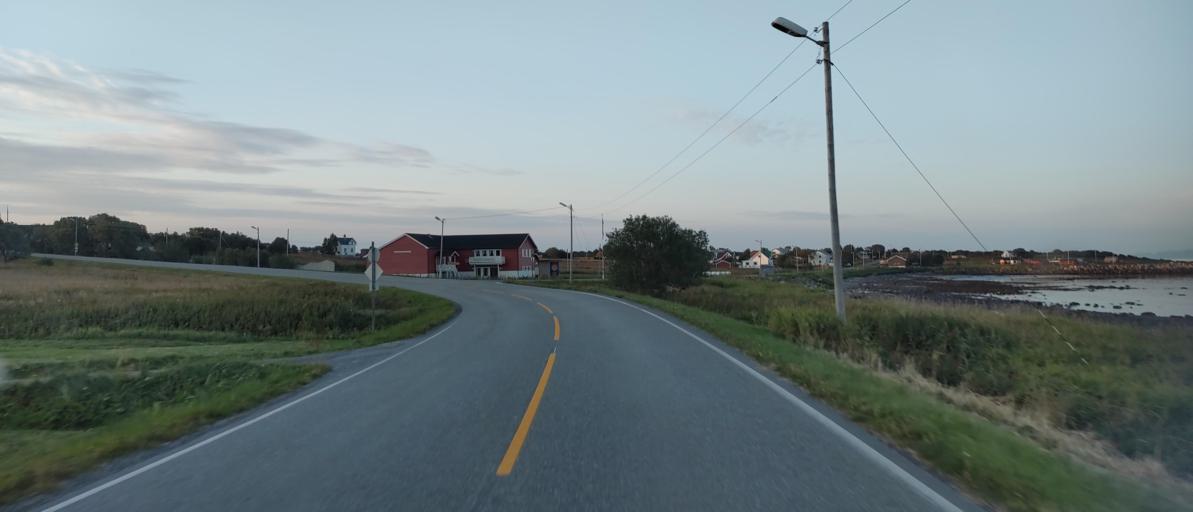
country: NO
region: Nordland
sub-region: Andoy
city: Andenes
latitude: 69.2438
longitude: 16.1183
